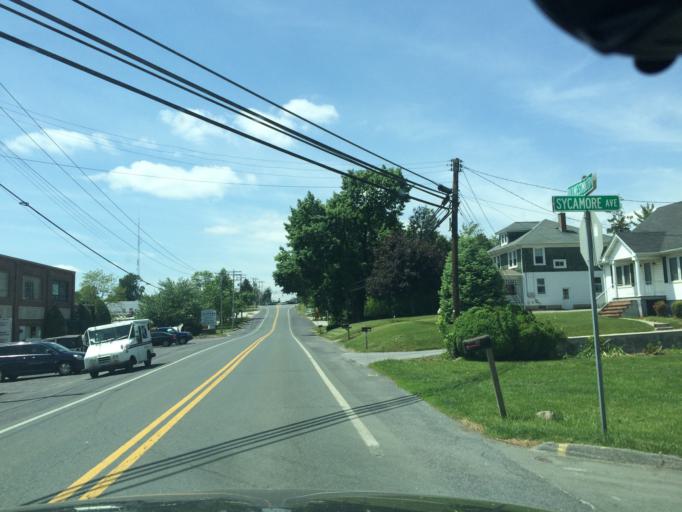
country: US
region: Maryland
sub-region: Carroll County
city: Westminster
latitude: 39.5605
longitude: -76.9768
